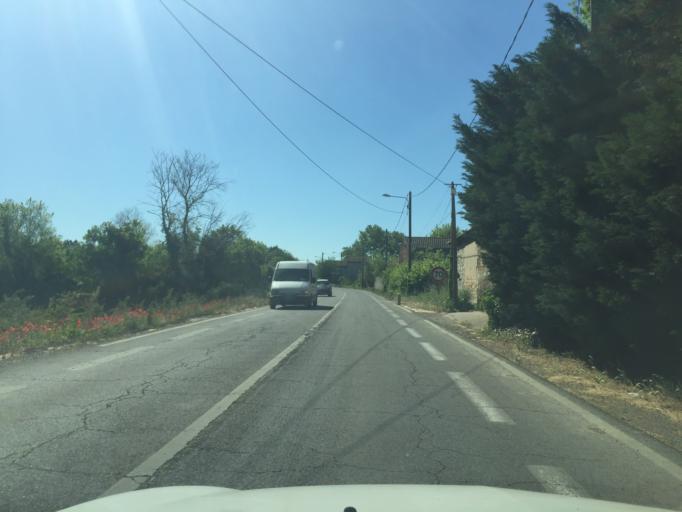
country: FR
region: Provence-Alpes-Cote d'Azur
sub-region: Departement du Vaucluse
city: Le Pontet
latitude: 43.9482
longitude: 4.8610
